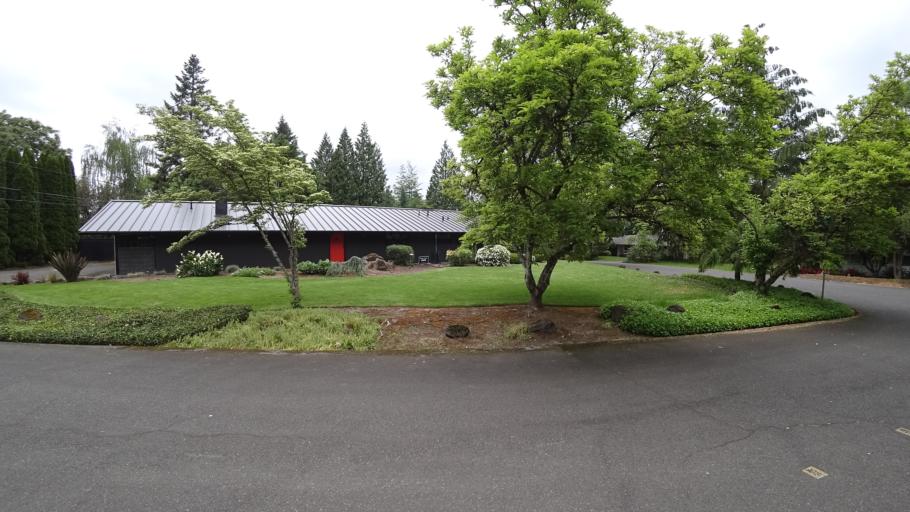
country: US
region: Oregon
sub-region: Washington County
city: Garden Home-Whitford
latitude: 45.4746
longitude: -122.7408
